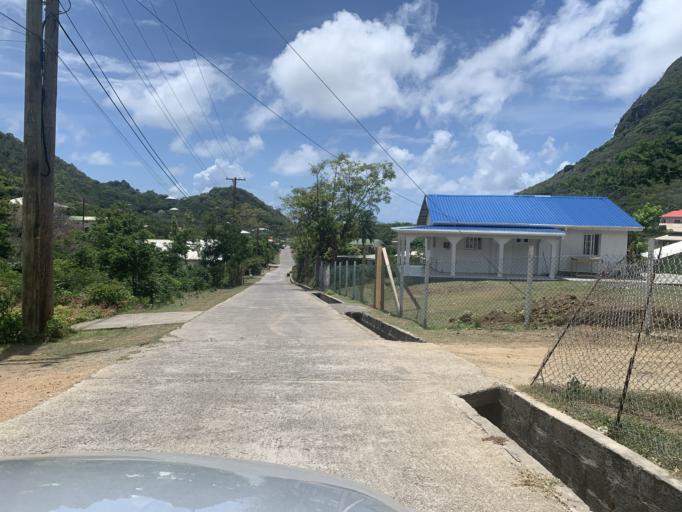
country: GD
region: Carriacou and Petite Martinique
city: Hillsborough
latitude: 12.6024
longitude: -61.4389
